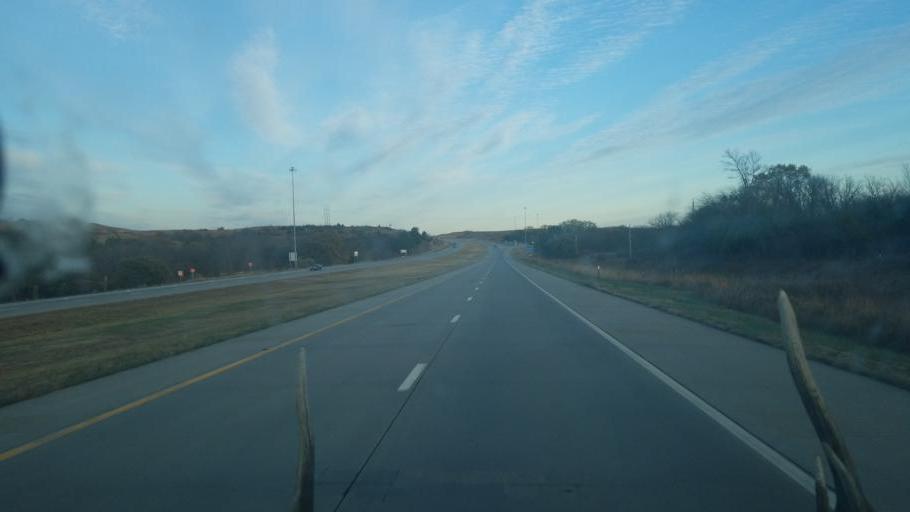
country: US
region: Kansas
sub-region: Riley County
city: Ogden
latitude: 39.0662
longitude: -96.6229
